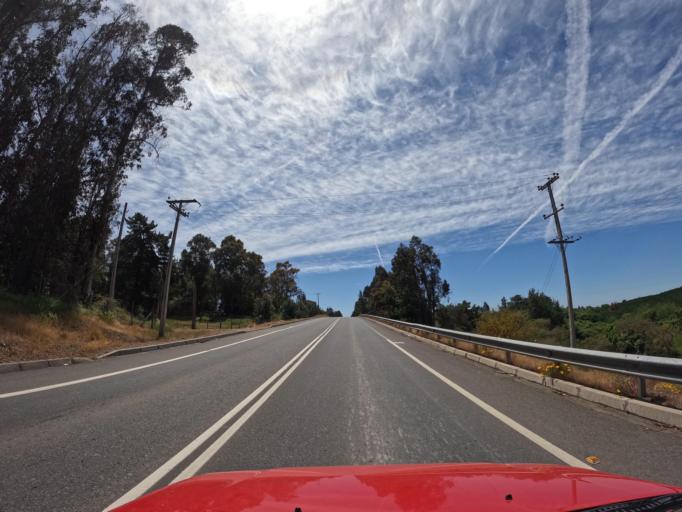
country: CL
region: Maule
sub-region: Provincia de Talca
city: Talca
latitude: -35.2894
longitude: -71.5312
